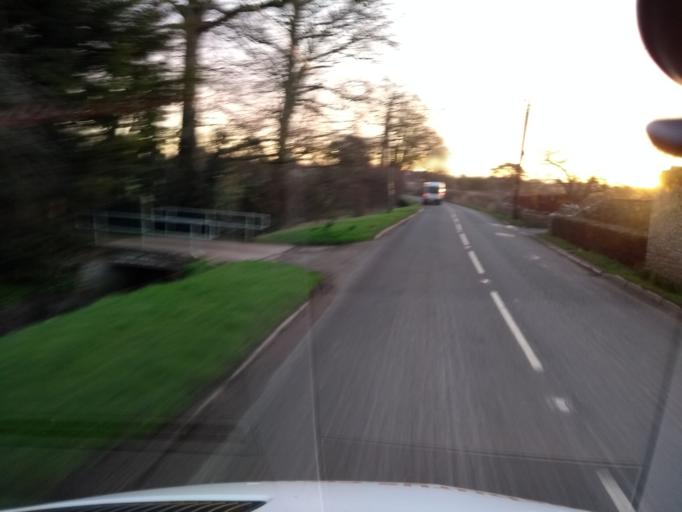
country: GB
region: England
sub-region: Somerset
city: Wedmore
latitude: 51.2249
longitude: -2.8558
